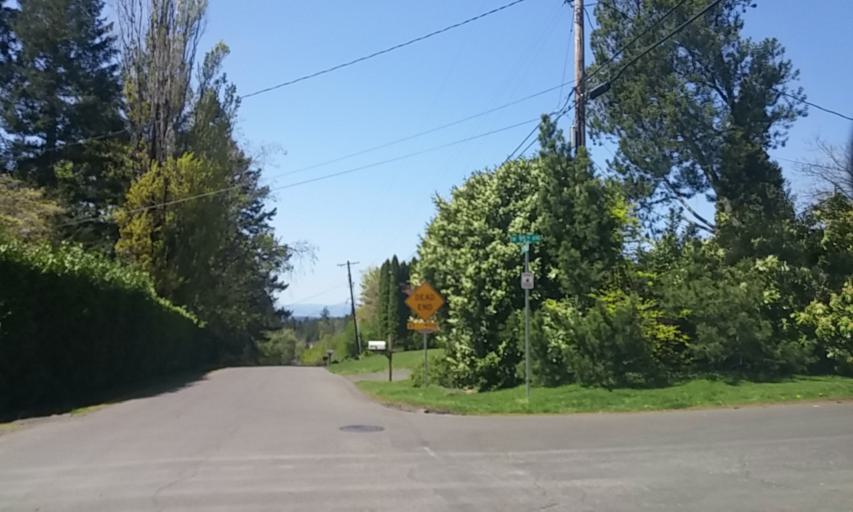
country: US
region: Oregon
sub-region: Washington County
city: West Haven
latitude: 45.5173
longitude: -122.7747
